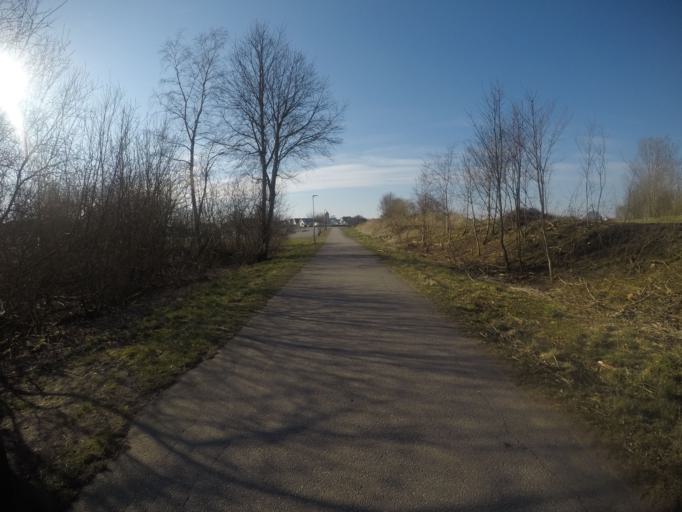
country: SE
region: Halland
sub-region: Laholms Kommun
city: Laholm
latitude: 56.5031
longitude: 13.0534
